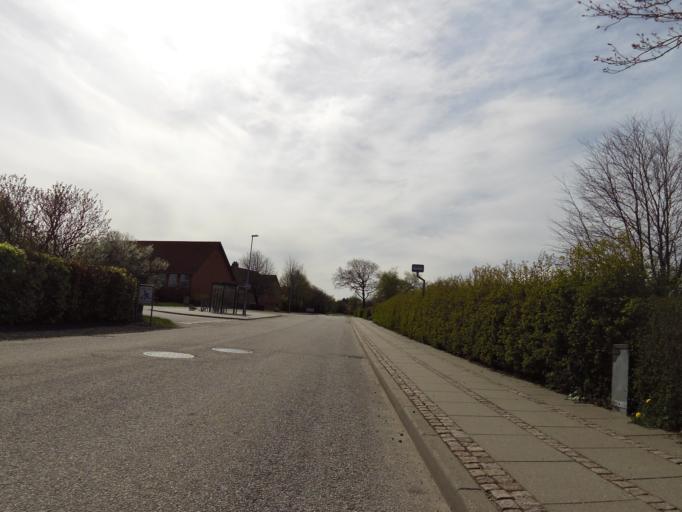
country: DK
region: Central Jutland
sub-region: Skive Kommune
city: Skive
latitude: 56.5352
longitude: 8.9413
